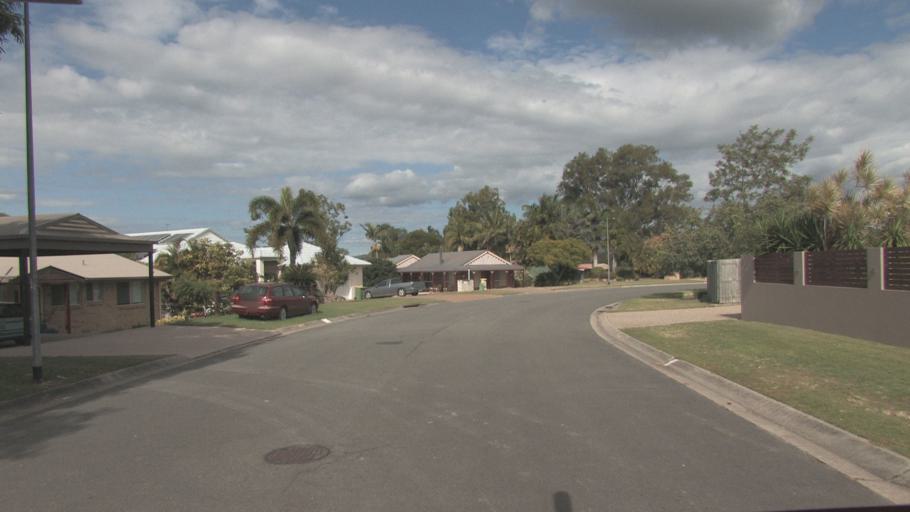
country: AU
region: Queensland
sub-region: Logan
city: Windaroo
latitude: -27.7373
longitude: 153.2040
